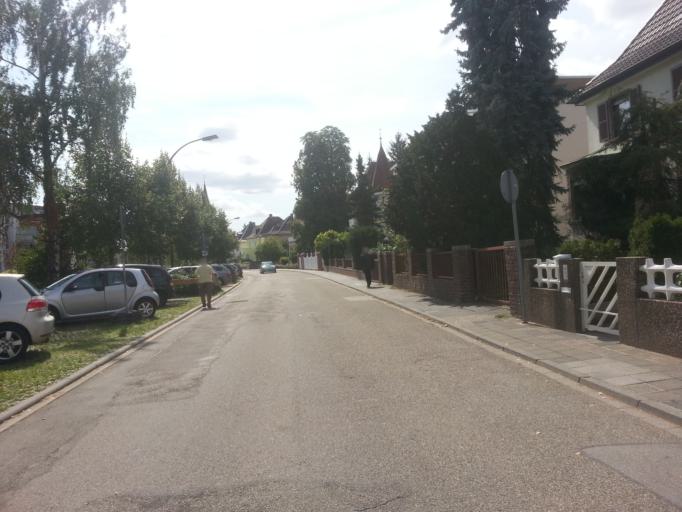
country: DE
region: Hesse
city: Viernheim
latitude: 49.5352
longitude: 8.5816
